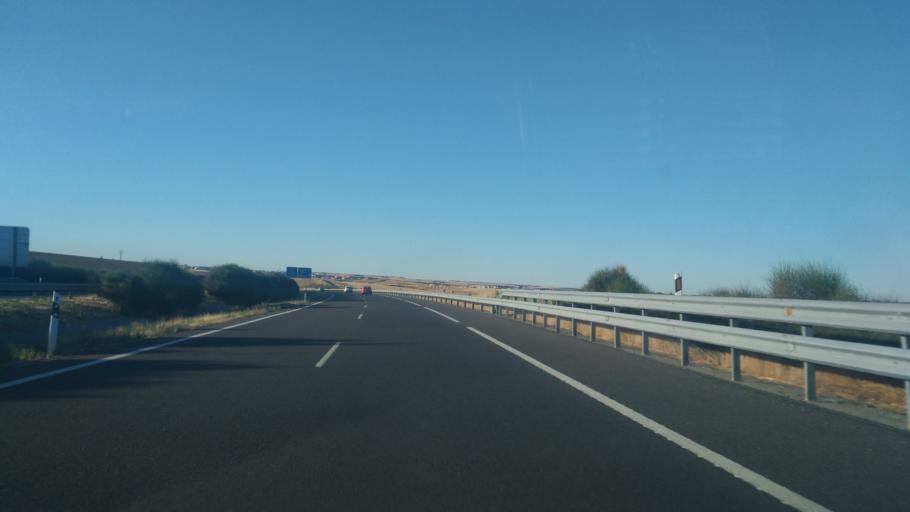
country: ES
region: Castille and Leon
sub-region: Provincia de Salamanca
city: Arapiles
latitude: 40.9077
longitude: -5.6611
